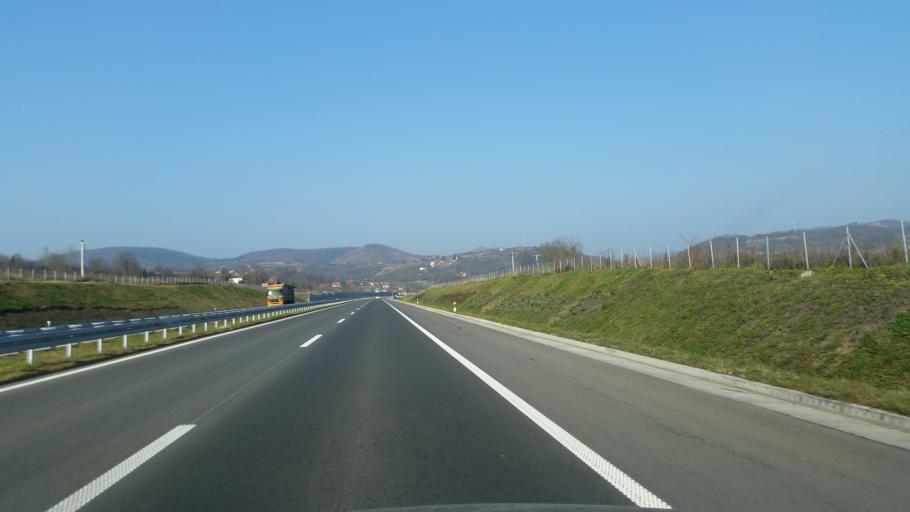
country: RS
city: Prislonica
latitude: 43.9572
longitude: 20.3987
